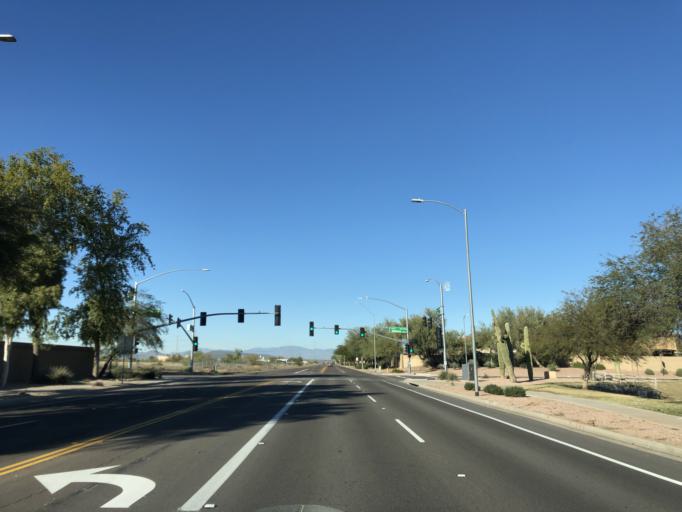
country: US
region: Arizona
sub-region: Maricopa County
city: Sun City West
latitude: 33.6883
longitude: -112.2897
